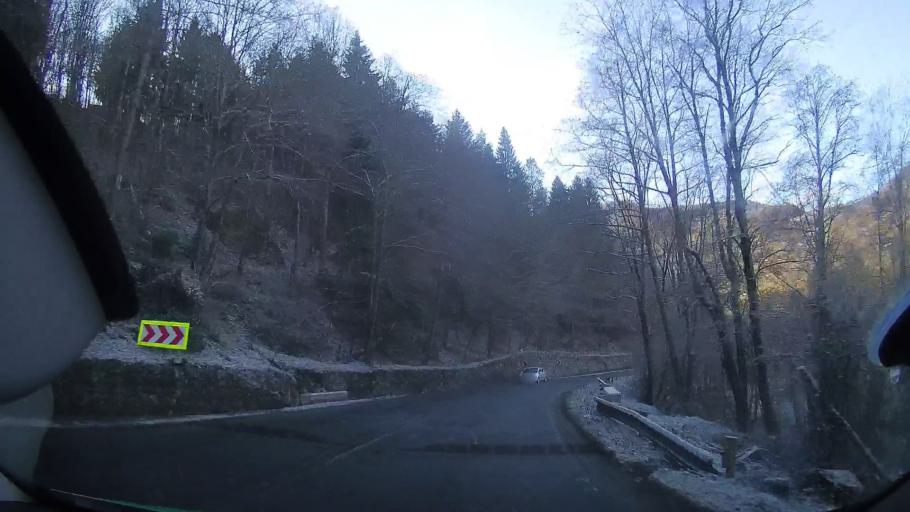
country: RO
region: Alba
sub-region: Comuna Sohodol
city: Sohodol
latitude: 46.3624
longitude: 23.0259
